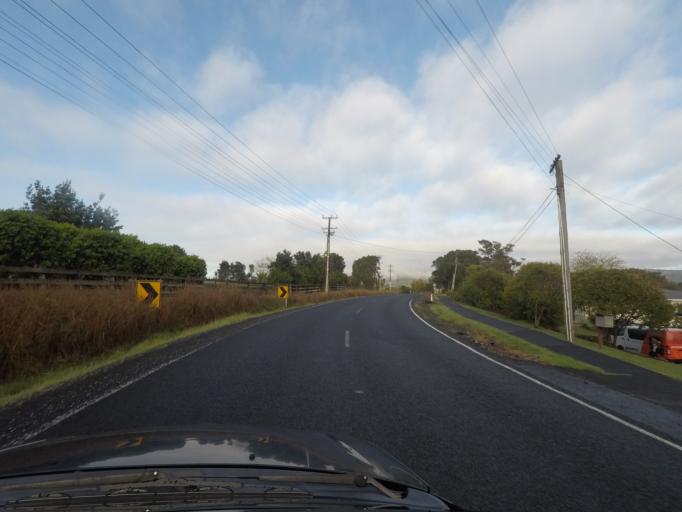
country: NZ
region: Auckland
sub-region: Auckland
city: Waitakere
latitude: -36.9044
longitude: 174.6123
